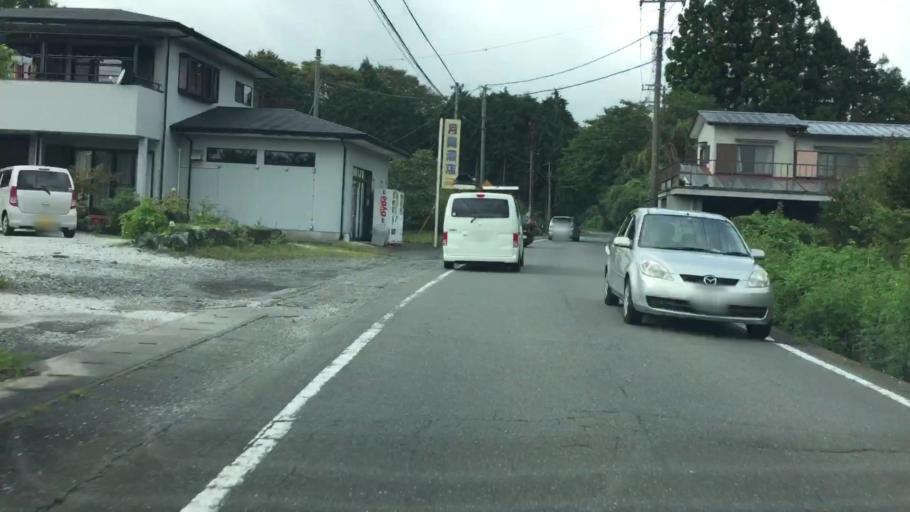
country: JP
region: Shizuoka
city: Fujinomiya
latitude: 35.3556
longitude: 138.5935
